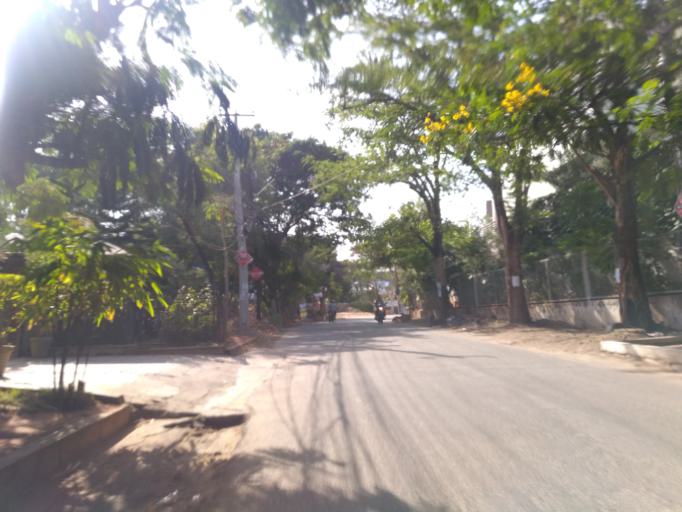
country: IN
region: Telangana
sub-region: Rangareddi
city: Kukatpalli
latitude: 17.4355
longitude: 78.4046
